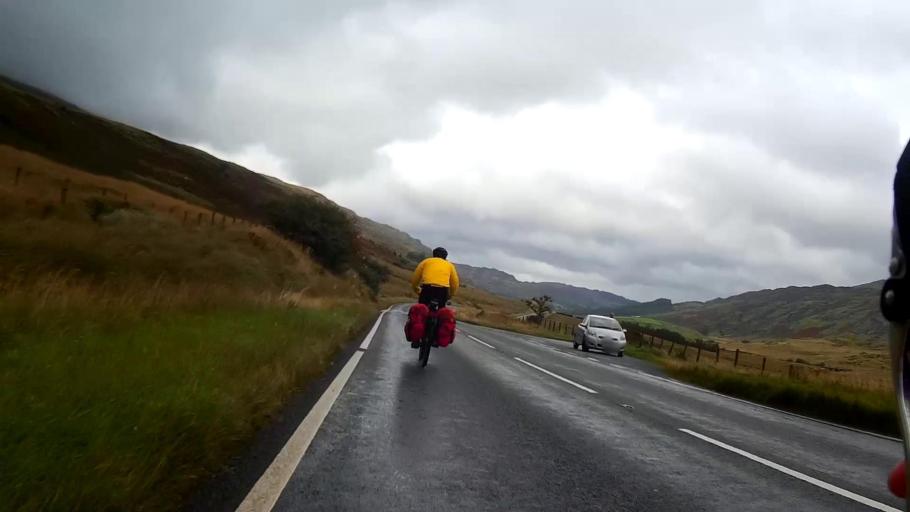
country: GB
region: Wales
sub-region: Gwynedd
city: Blaenau-Ffestiniog
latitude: 53.0904
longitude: -3.9651
